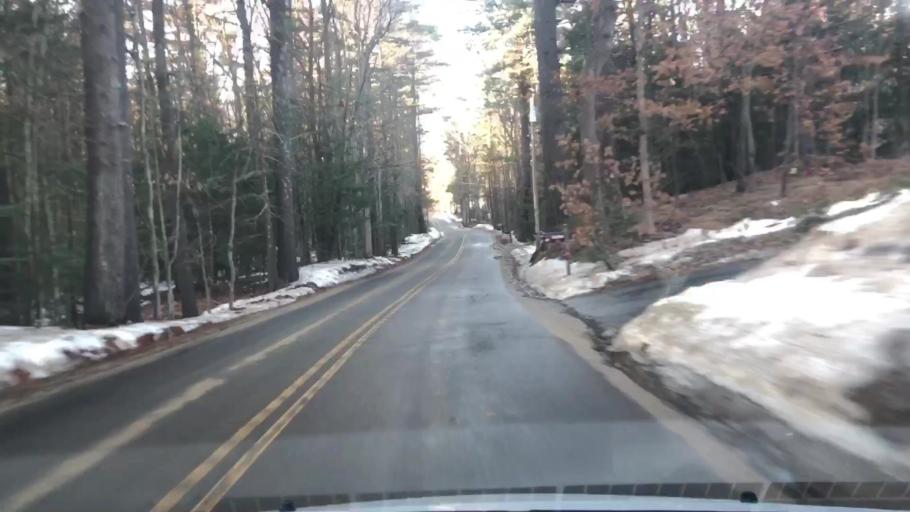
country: US
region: New Hampshire
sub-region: Hillsborough County
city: Milford
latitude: 42.8029
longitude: -71.6464
